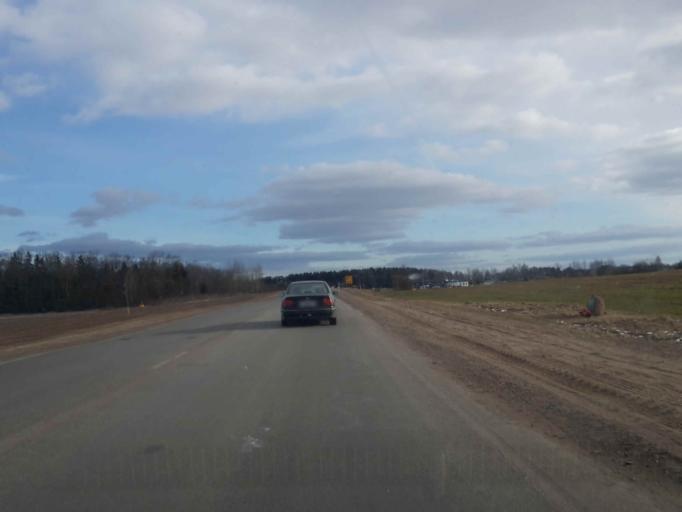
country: BY
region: Minsk
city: Bal'shavik
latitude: 54.0738
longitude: 27.5654
